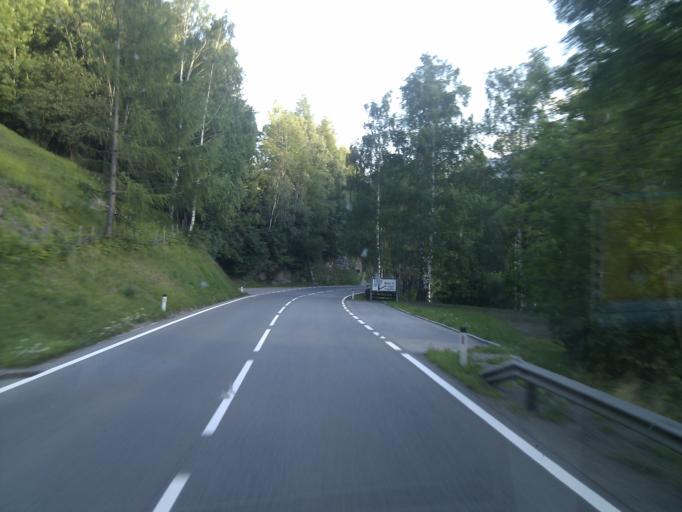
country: AT
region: Tyrol
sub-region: Politischer Bezirk Lienz
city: Matrei in Osttirol
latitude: 47.0080
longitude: 12.5401
